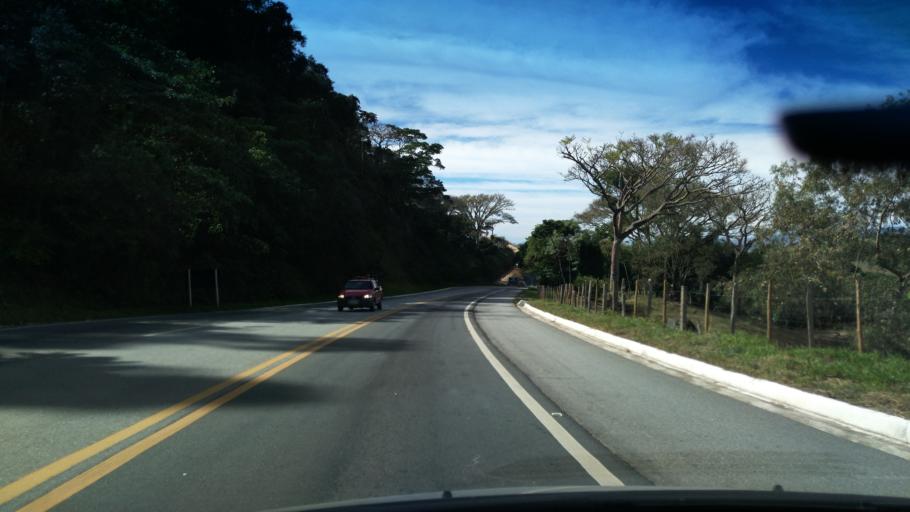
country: BR
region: Minas Gerais
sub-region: Borda Da Mata
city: Borda da Mata
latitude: -22.1345
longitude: -46.1722
